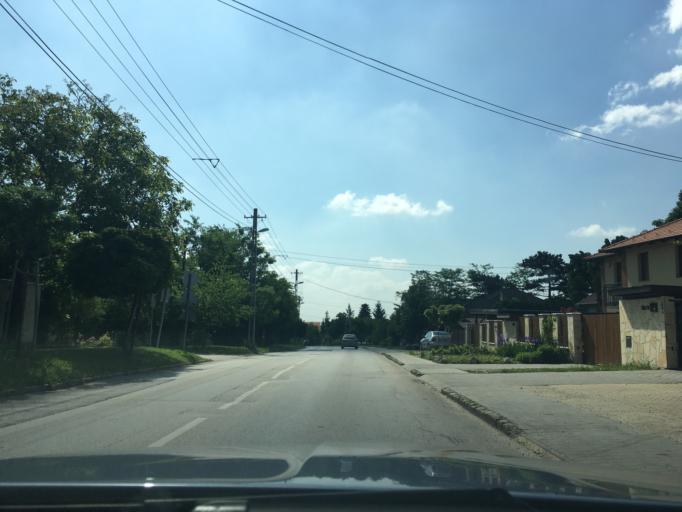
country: HU
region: Budapest
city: Budapest XXII. keruelet
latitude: 47.4203
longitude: 19.0143
